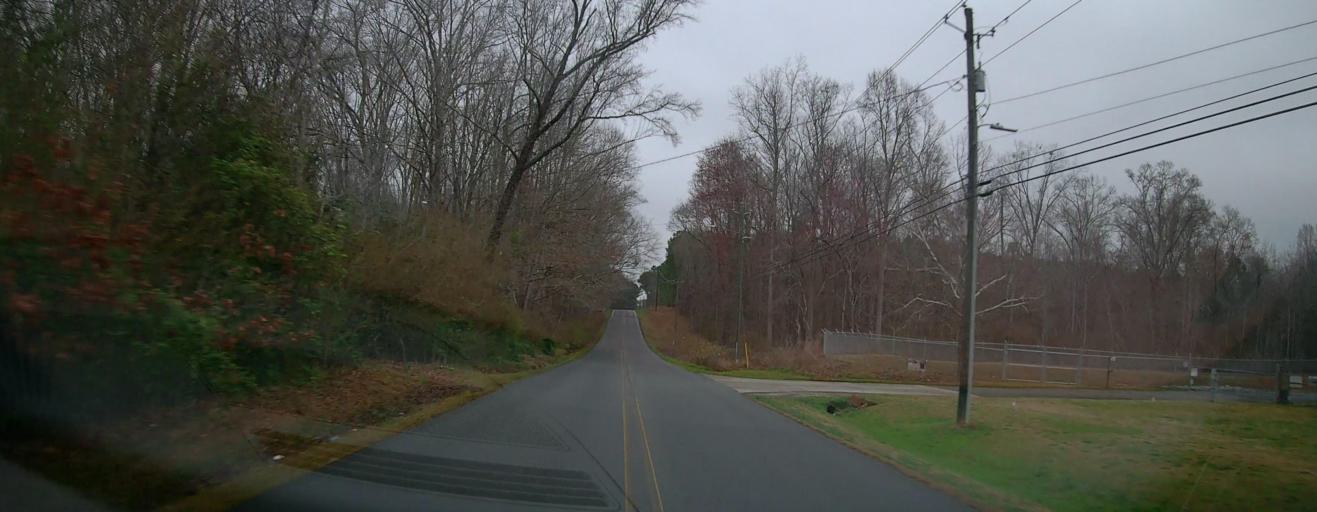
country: US
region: Georgia
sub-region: Pike County
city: Zebulon
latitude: 33.1154
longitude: -84.3434
